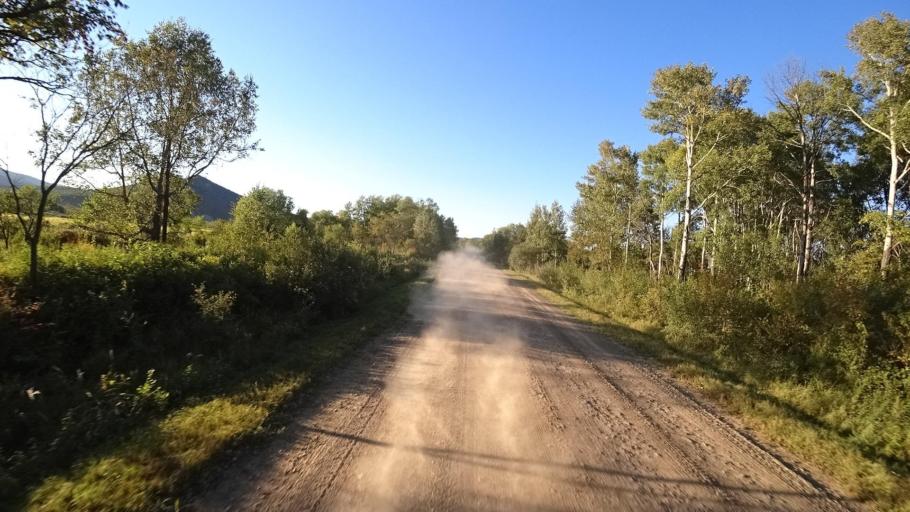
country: RU
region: Primorskiy
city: Kirovskiy
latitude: 44.8294
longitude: 133.5900
